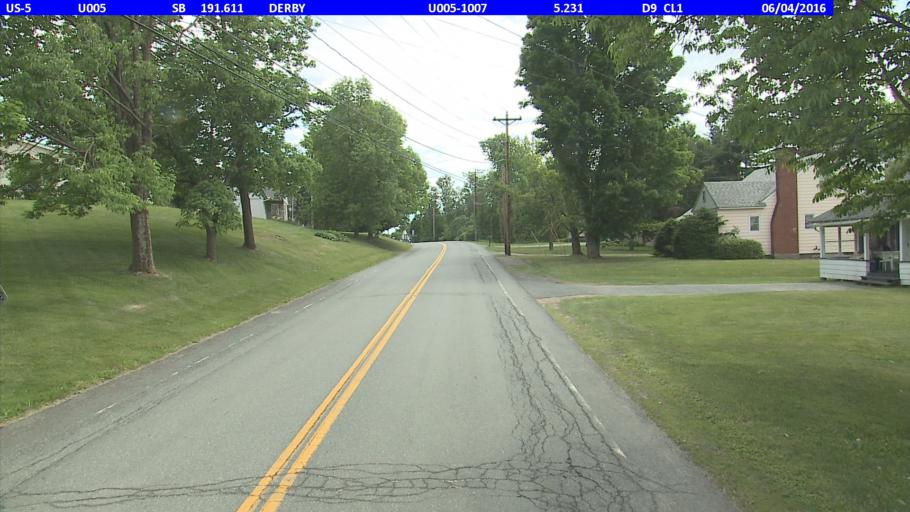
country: US
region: Vermont
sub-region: Orleans County
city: Newport
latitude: 44.9965
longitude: -72.1056
